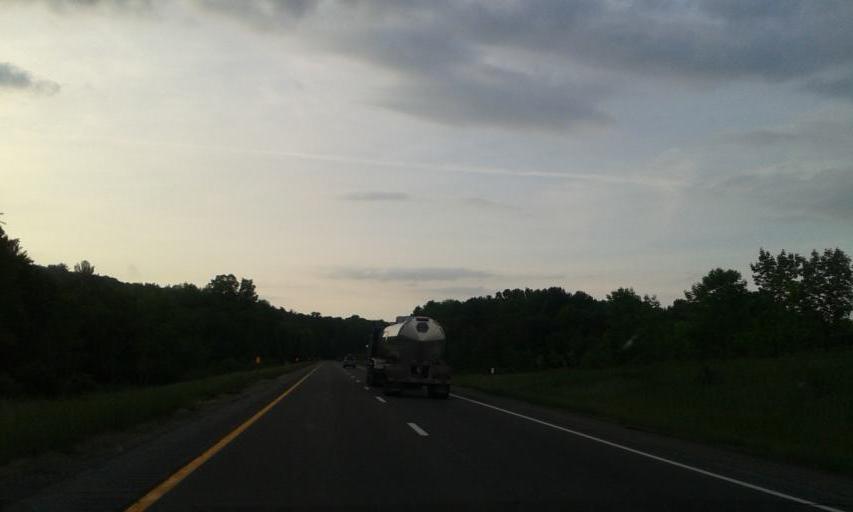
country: US
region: New York
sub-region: Broome County
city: Chenango Bridge
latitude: 42.2738
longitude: -75.9235
